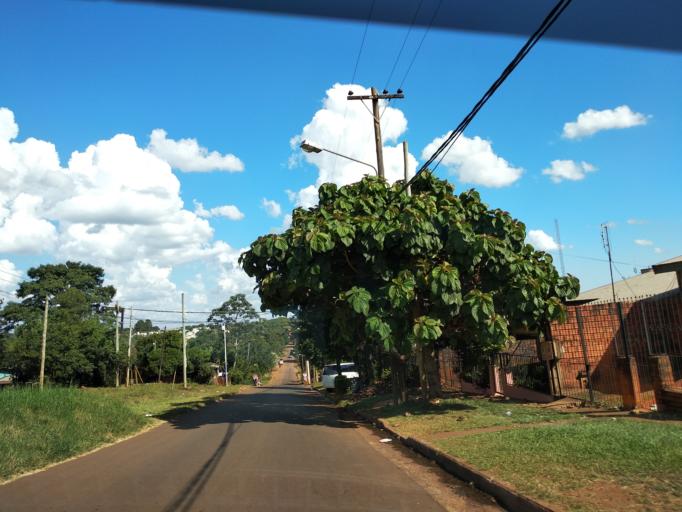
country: AR
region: Misiones
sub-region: Departamento de Capital
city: Posadas
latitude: -27.3854
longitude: -55.9457
